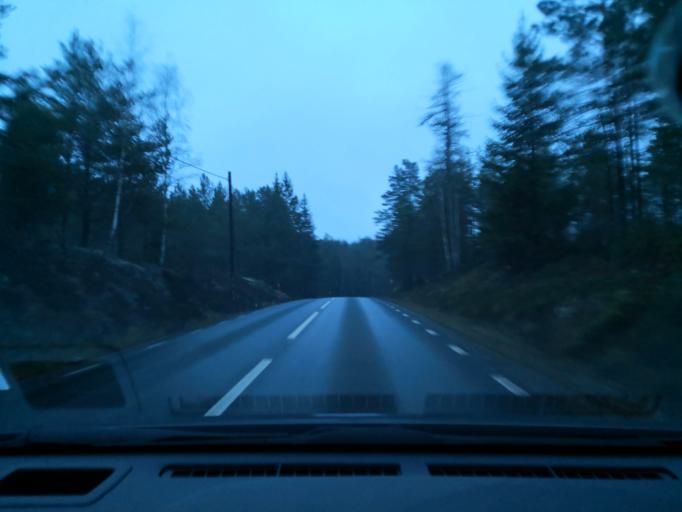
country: SE
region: Soedermanland
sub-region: Eskilstuna Kommun
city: Skogstorp
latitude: 59.2525
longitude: 16.3501
